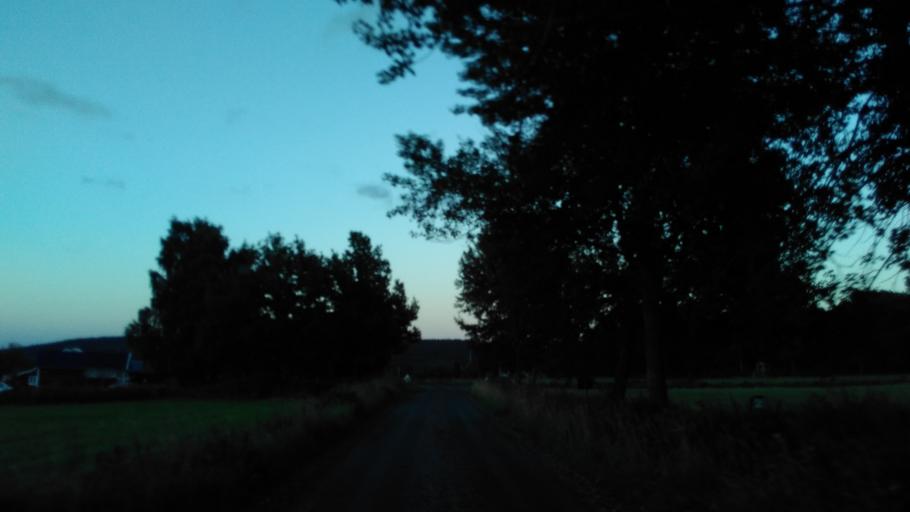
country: SE
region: Vaestra Goetaland
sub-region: Vargarda Kommun
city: Jonstorp
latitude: 57.9639
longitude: 12.7175
